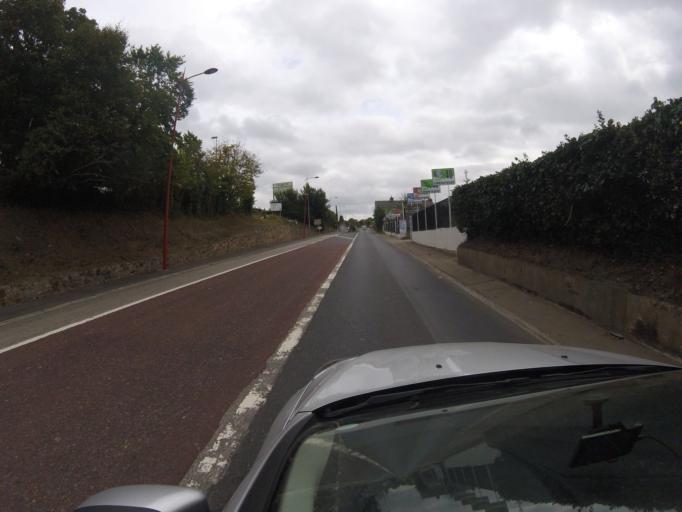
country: FR
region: Lower Normandy
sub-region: Departement de la Manche
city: Cherbourg-Octeville
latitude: 49.6164
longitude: -1.6072
